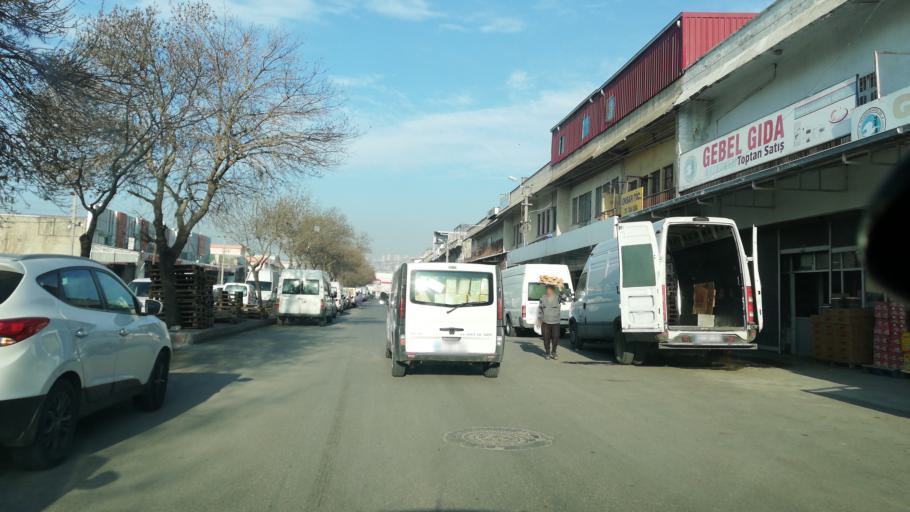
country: TR
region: Kahramanmaras
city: Kahramanmaras
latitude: 37.5645
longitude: 36.9206
